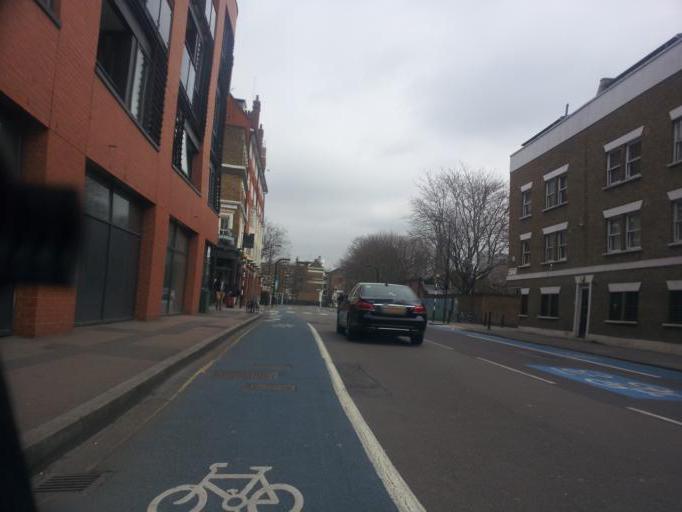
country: GB
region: England
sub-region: Greater London
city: City of London
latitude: 51.5014
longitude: -0.0983
